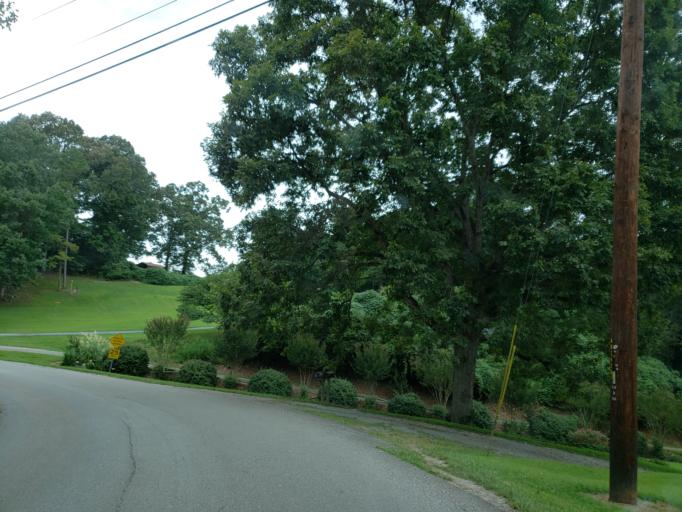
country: US
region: Georgia
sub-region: Gilmer County
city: Ellijay
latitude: 34.6419
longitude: -84.4996
